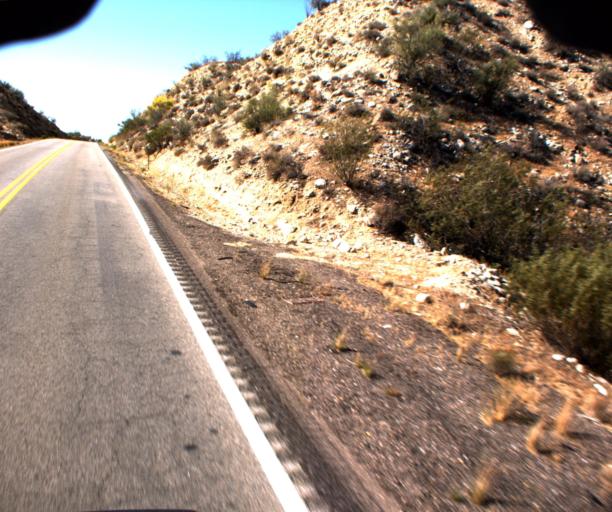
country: US
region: Arizona
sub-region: Yavapai County
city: Bagdad
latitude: 34.7973
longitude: -113.6240
